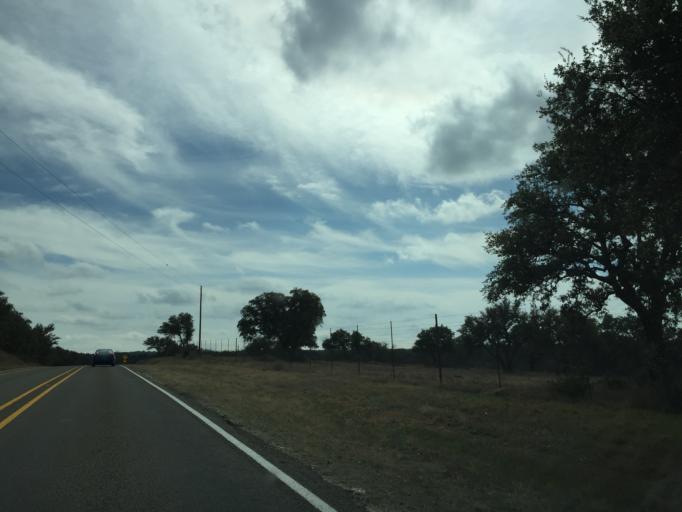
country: US
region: Texas
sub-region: Burnet County
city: Granite Shoals
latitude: 30.5149
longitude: -98.4429
